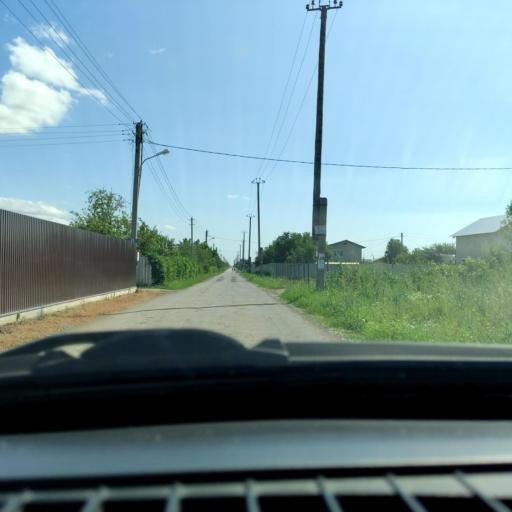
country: RU
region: Samara
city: Tol'yatti
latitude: 53.7354
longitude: 49.3965
